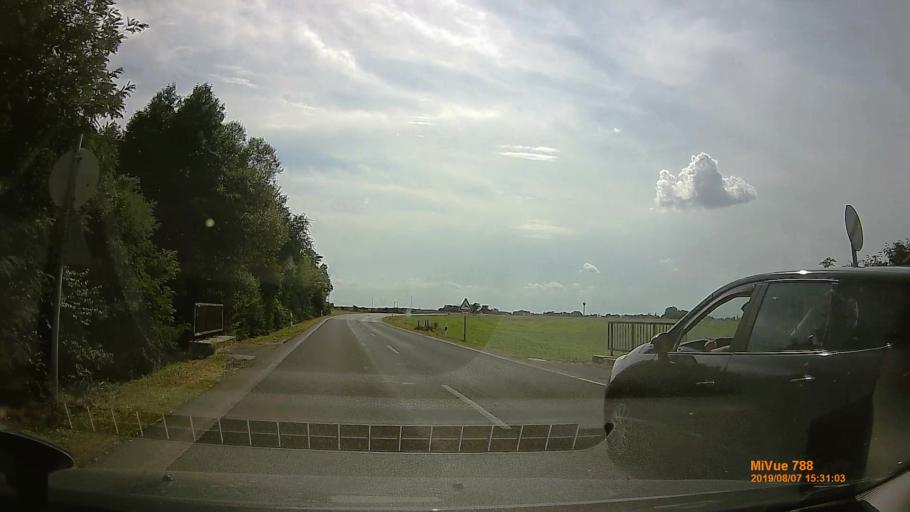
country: HU
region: Vas
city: Vep
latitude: 47.2728
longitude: 16.7570
